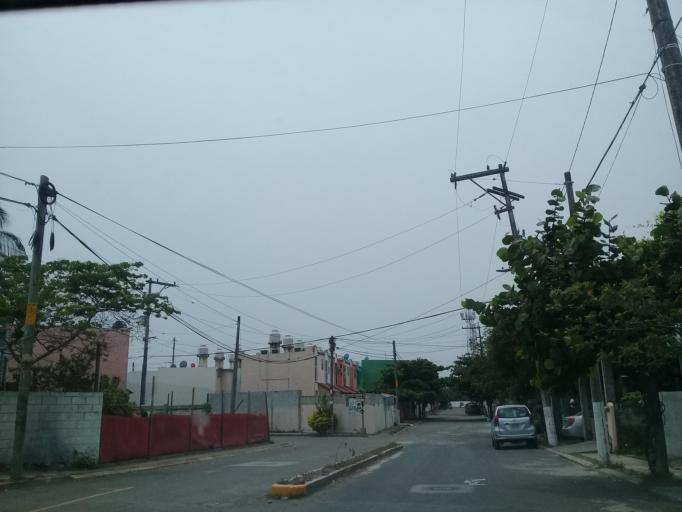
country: MX
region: Veracruz
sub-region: Veracruz
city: Las Amapolas
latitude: 19.1529
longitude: -96.2040
